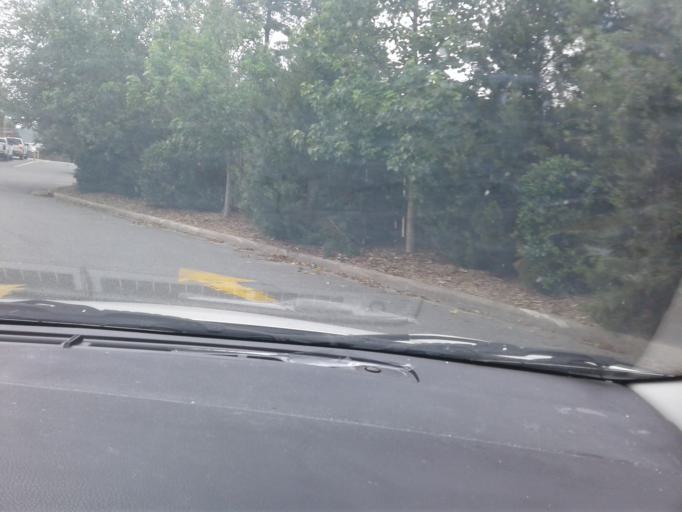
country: US
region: North Carolina
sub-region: Harnett County
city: Dunn
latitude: 35.3151
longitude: -78.6257
